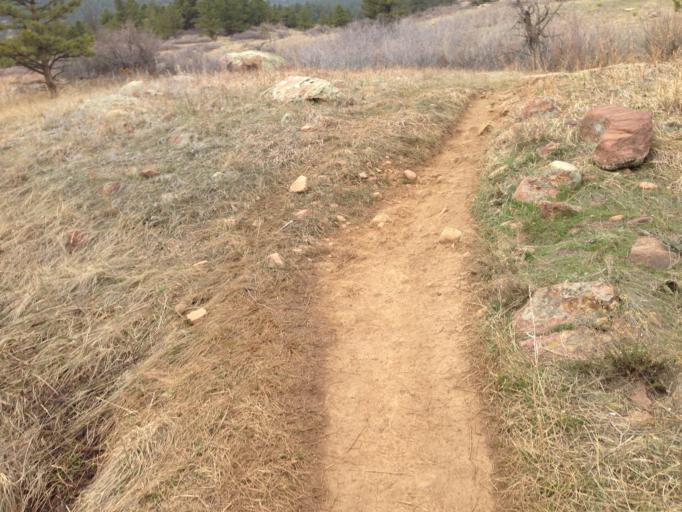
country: US
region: Colorado
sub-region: Boulder County
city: Boulder
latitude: 39.9482
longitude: -105.2671
